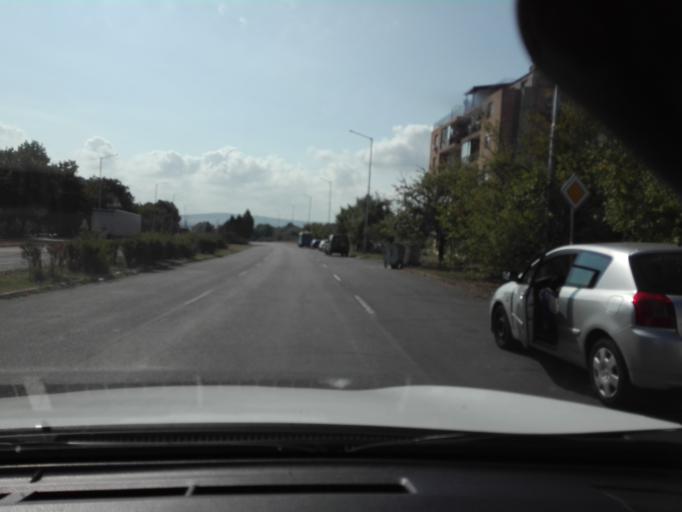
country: BG
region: Burgas
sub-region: Obshtina Burgas
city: Burgas
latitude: 42.4524
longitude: 27.4207
